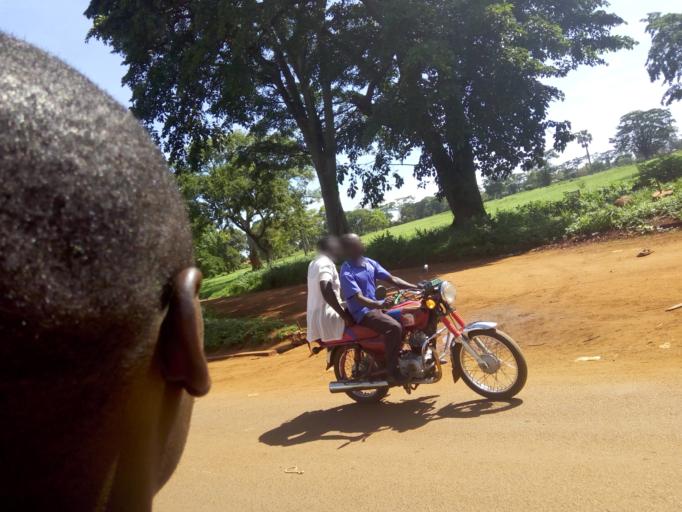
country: UG
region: Western Region
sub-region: Masindi District
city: Masindi
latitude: 1.6871
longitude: 31.7169
